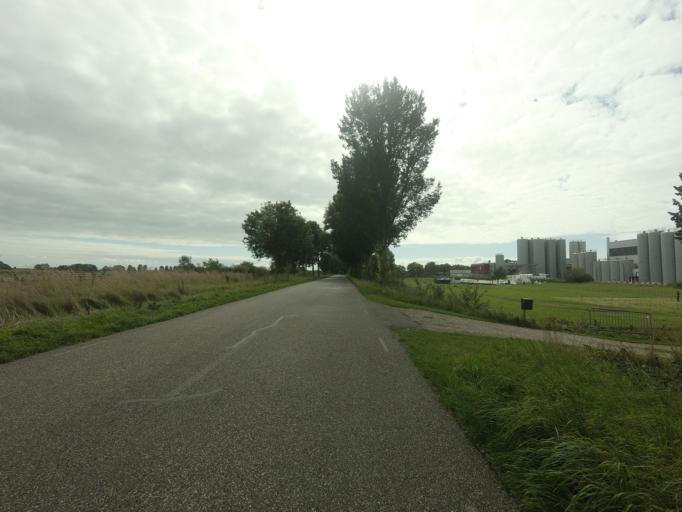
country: NL
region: Friesland
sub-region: Sudwest Fryslan
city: Workum
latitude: 52.9741
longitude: 5.4586
